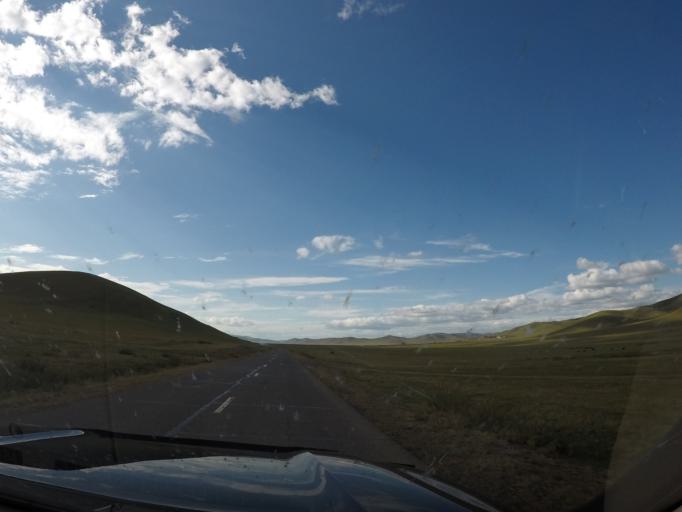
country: MN
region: Hentiy
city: Modot
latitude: 47.6987
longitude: 109.0787
